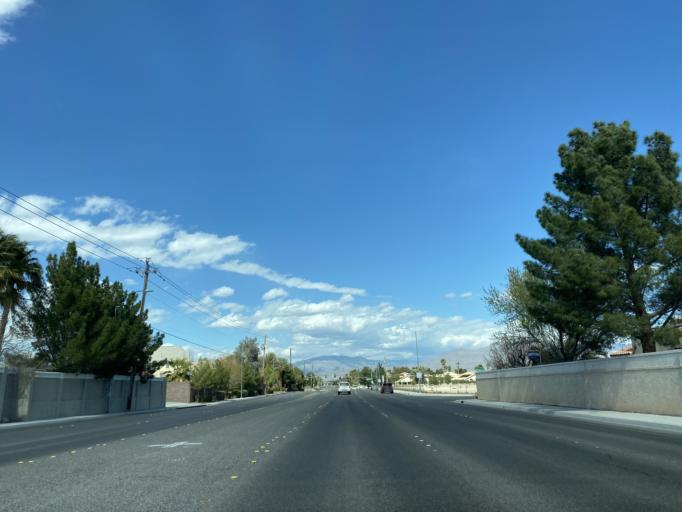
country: US
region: Nevada
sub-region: Clark County
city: Spring Valley
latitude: 36.2380
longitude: -115.2605
